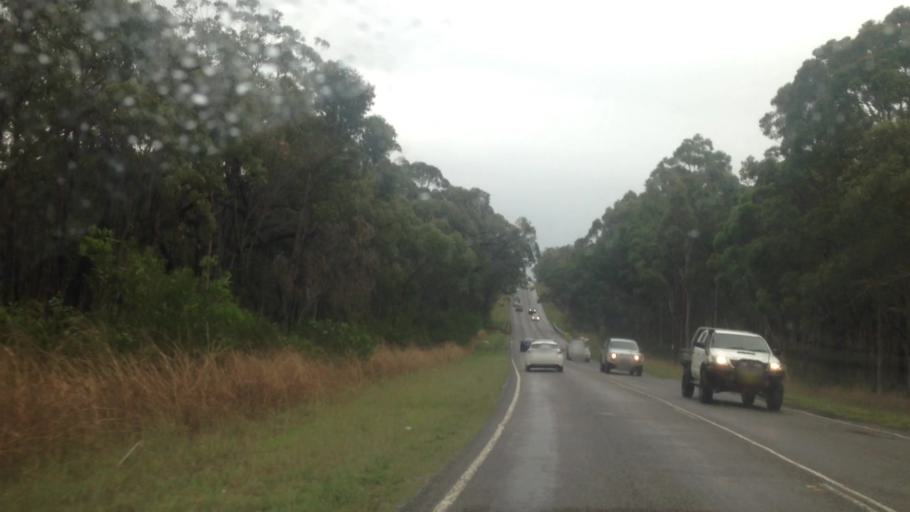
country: AU
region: New South Wales
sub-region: Lake Macquarie Shire
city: Dora Creek
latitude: -33.1476
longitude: 151.4792
